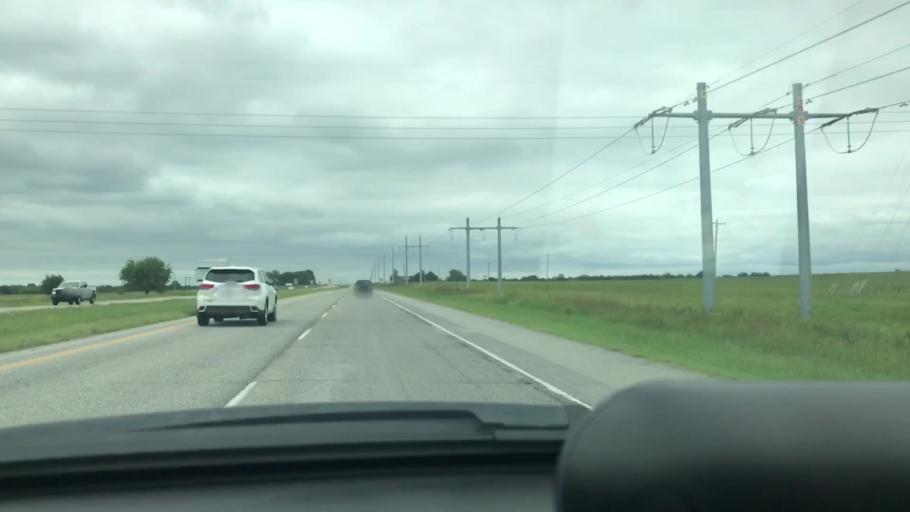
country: US
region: Oklahoma
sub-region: Wagoner County
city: Wagoner
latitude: 36.0077
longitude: -95.3685
